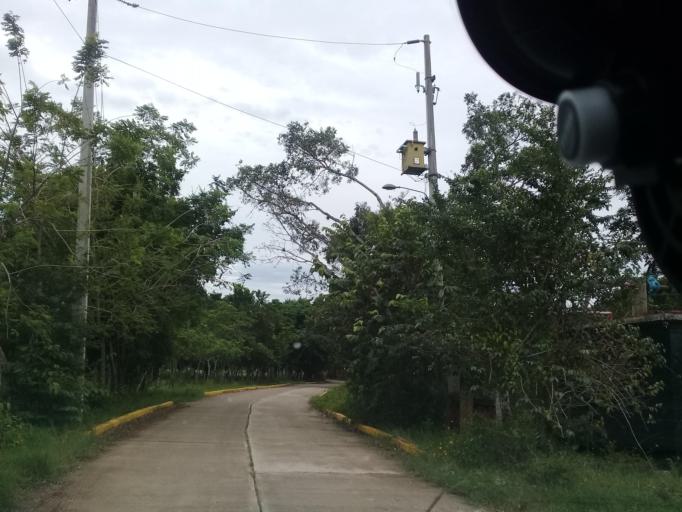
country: MX
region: Hidalgo
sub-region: Huejutla de Reyes
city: Chalahuiyapa
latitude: 21.1628
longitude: -98.3640
